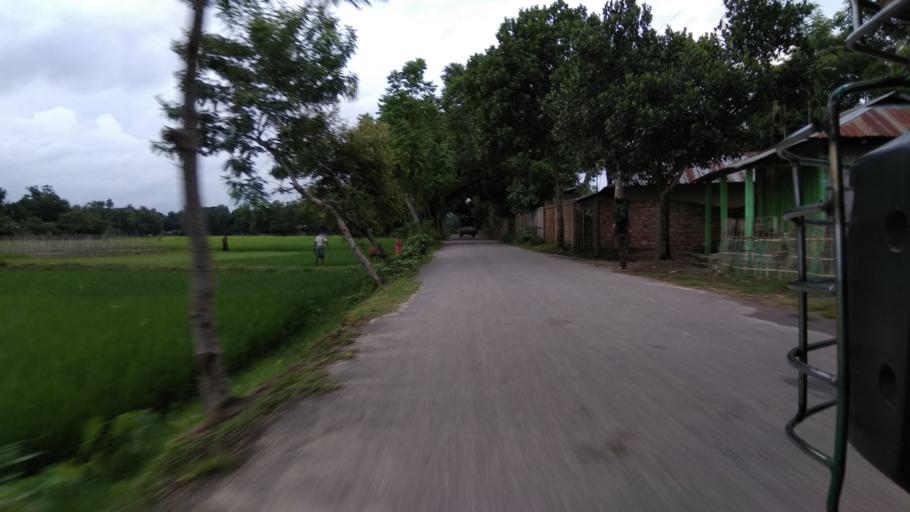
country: IN
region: Tripura
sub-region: Dhalai
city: Kamalpur
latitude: 24.2160
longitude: 91.8550
